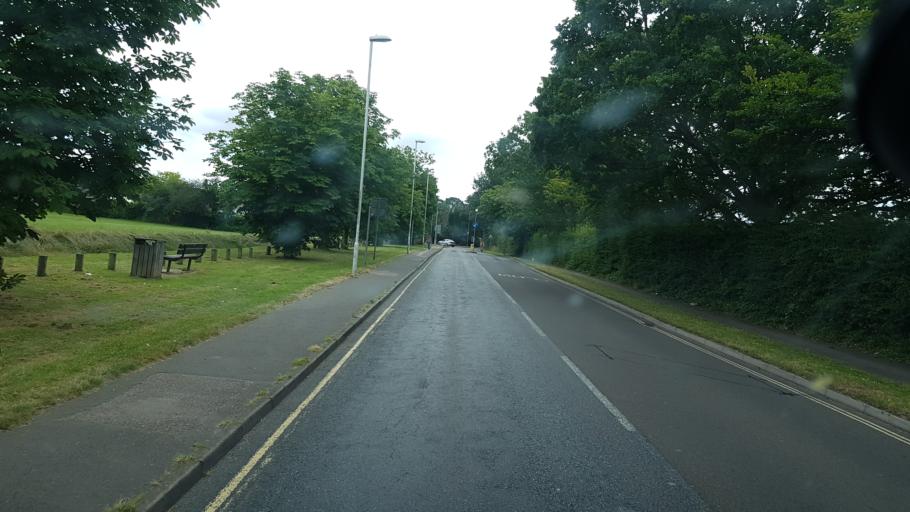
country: GB
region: England
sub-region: Surrey
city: Felbridge
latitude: 51.1335
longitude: -0.0333
